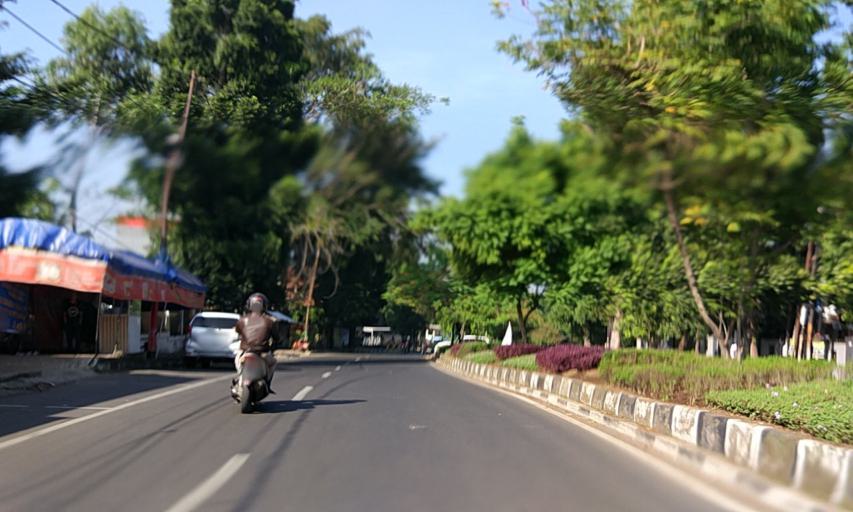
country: ID
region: West Java
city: Bandung
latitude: -6.8811
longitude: 107.6160
